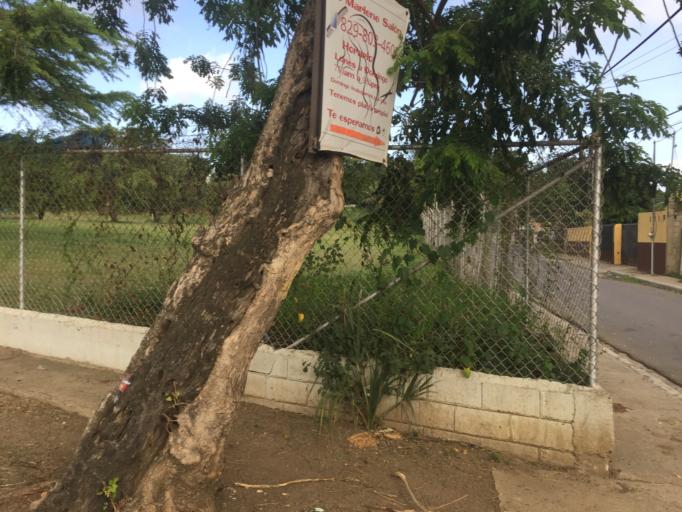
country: DO
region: Santiago
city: Santiago de los Caballeros
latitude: 19.4103
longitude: -70.7183
